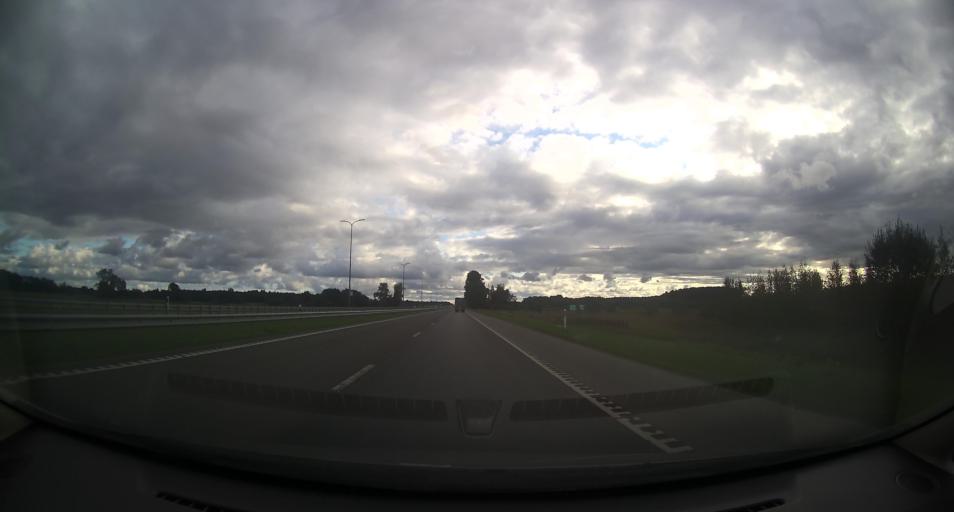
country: EE
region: Harju
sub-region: Saue vald
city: Laagri
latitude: 59.3353
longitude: 24.5869
